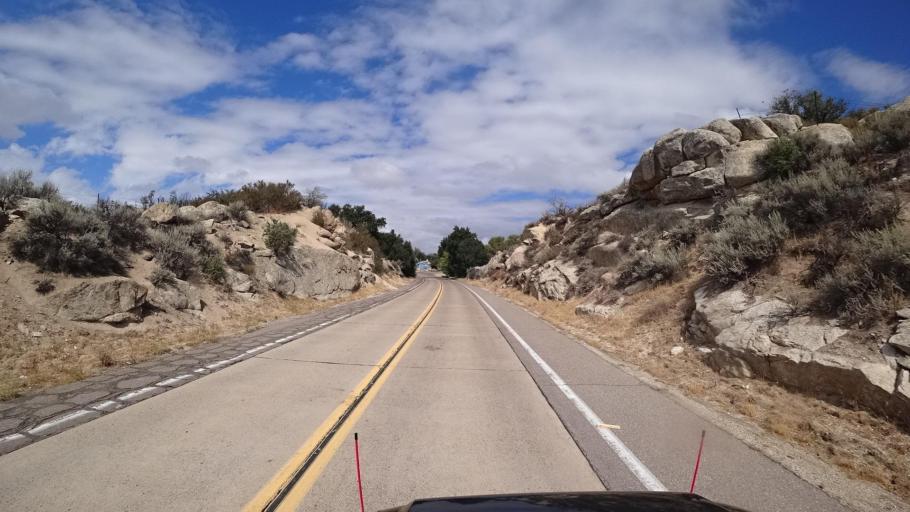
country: US
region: California
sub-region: San Diego County
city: Campo
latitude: 32.6853
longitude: -116.3352
